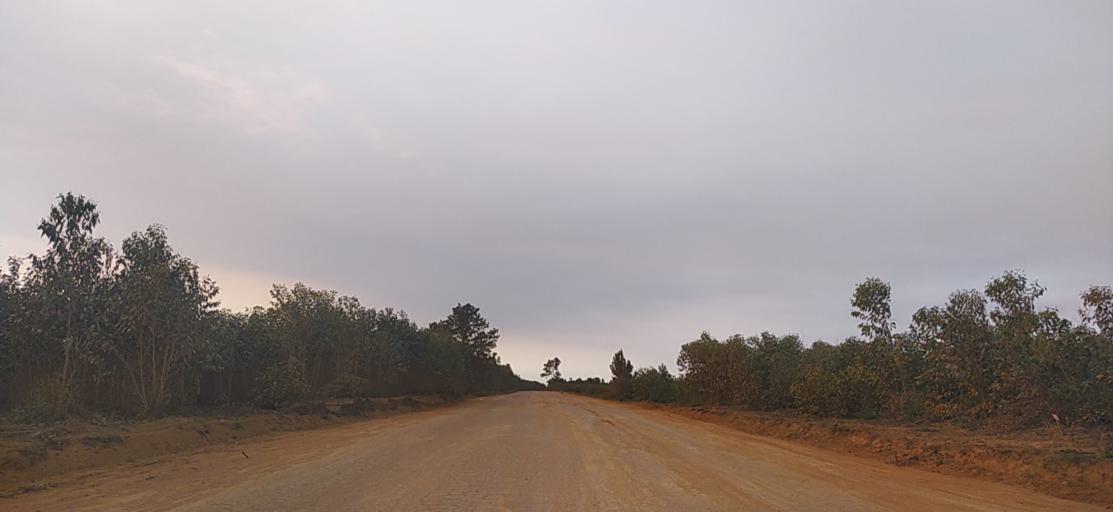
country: MG
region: Analamanga
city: Anjozorobe
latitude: -18.4728
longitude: 48.2619
